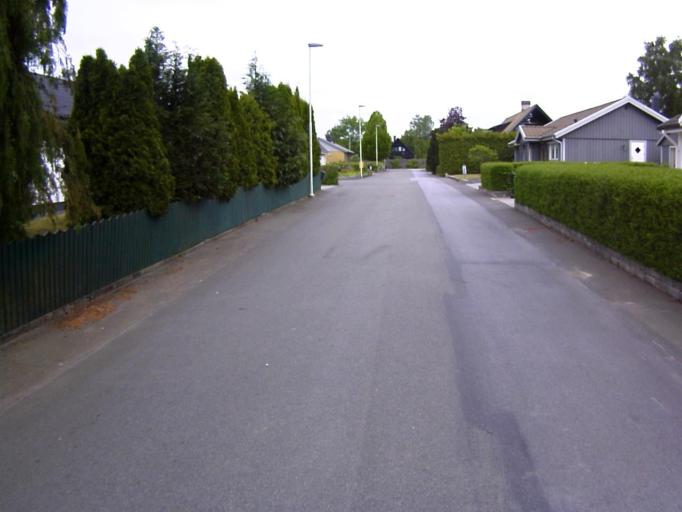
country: SE
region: Skane
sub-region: Kristianstads Kommun
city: Ahus
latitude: 55.9350
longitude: 14.2938
